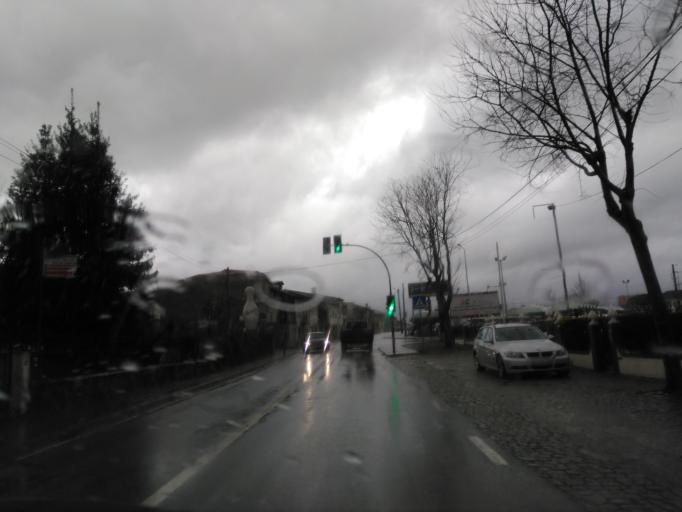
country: PT
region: Braga
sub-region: Braga
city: Braga
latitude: 41.5640
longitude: -8.4497
